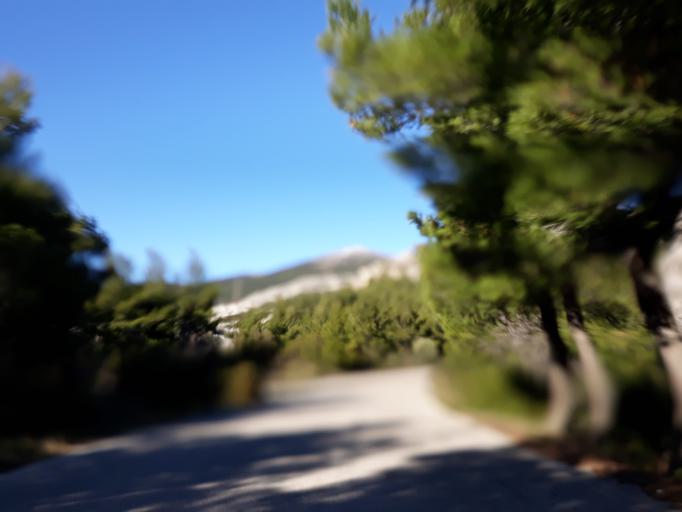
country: GR
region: Attica
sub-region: Nomarchia Dytikis Attikis
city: Fyli
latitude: 38.1281
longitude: 23.6471
